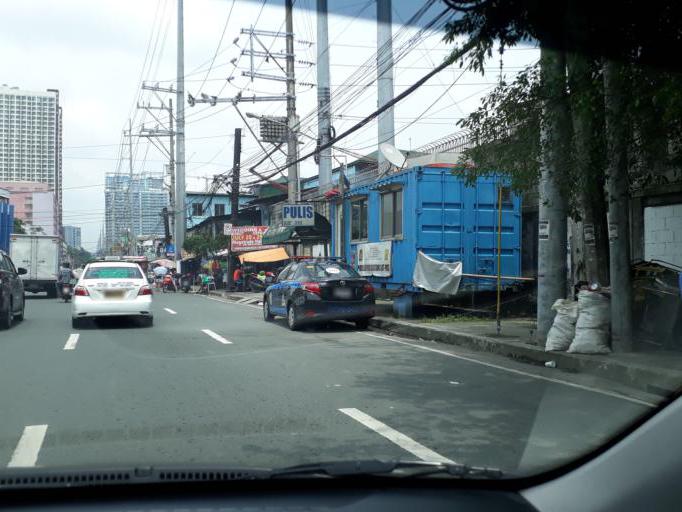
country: PH
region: Calabarzon
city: Del Monte
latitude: 14.6189
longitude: 121.0155
